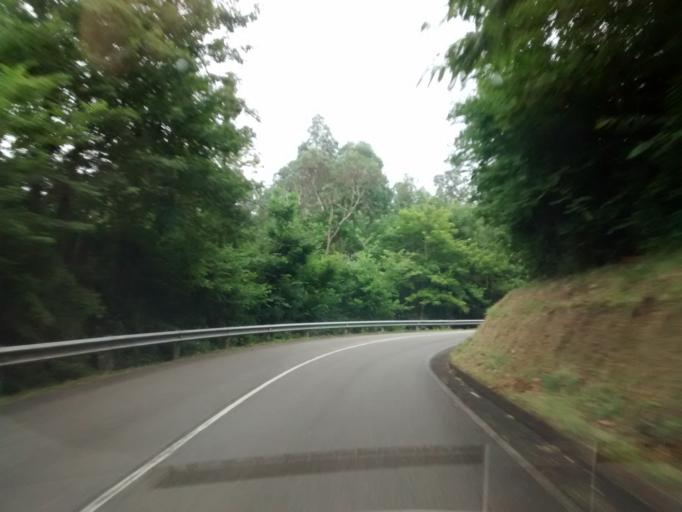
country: ES
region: Asturias
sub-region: Province of Asturias
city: Villaviciosa
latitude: 43.5401
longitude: -5.4047
